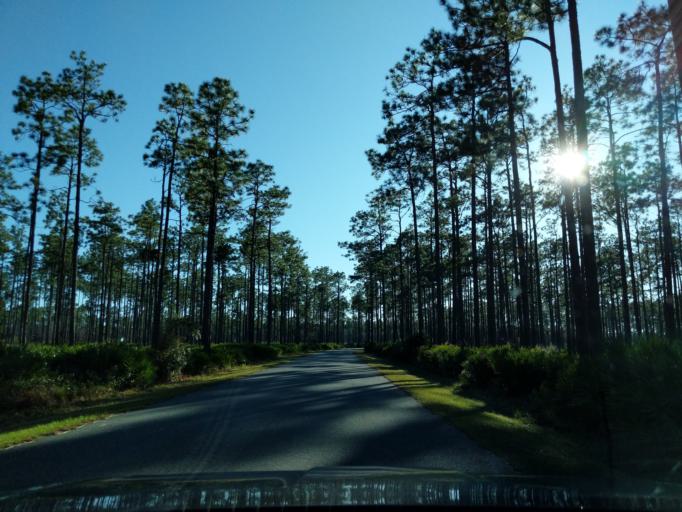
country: US
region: Georgia
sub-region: Charlton County
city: Folkston
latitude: 30.7102
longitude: -82.1445
